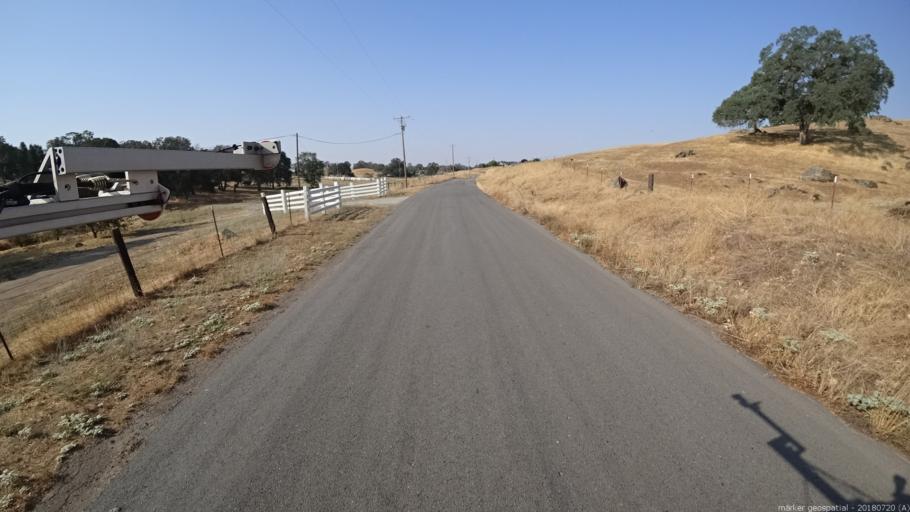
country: US
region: California
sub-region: Madera County
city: Yosemite Lakes
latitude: 37.2314
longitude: -119.9083
